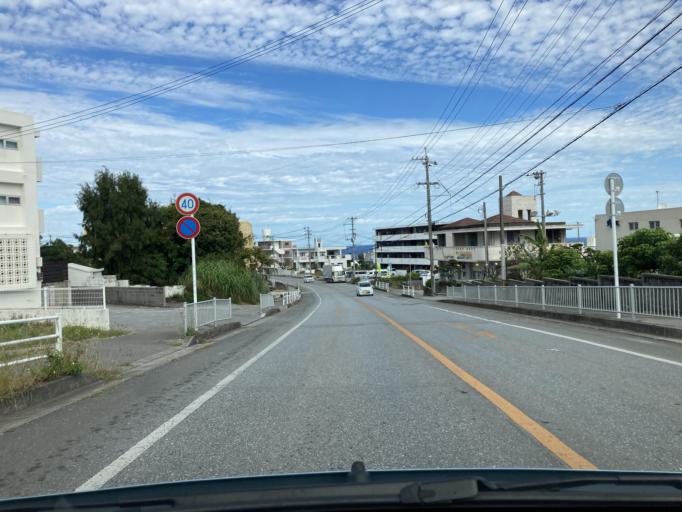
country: JP
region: Okinawa
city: Ishikawa
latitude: 26.4187
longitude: 127.7324
